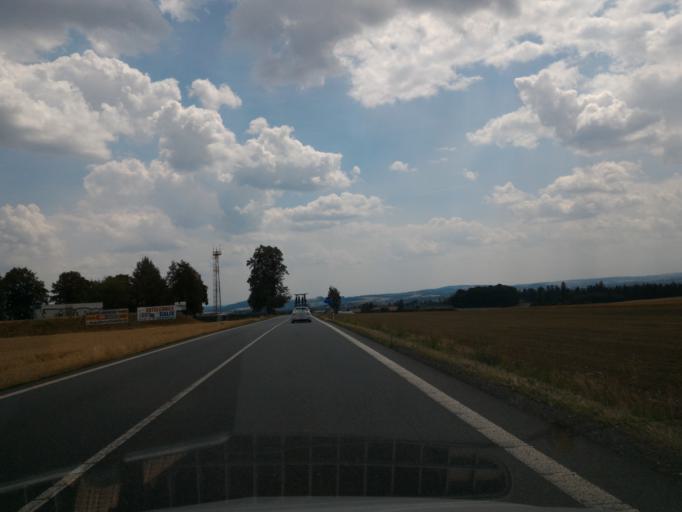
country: CZ
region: Vysocina
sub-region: Okres Havlickuv Brod
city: Havlickuv Brod
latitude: 49.6352
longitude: 15.5664
